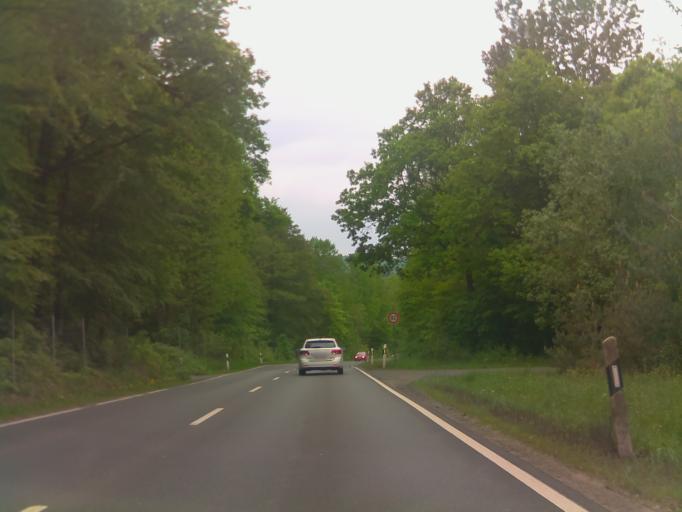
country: DE
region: Hesse
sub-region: Regierungsbezirk Darmstadt
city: Kronberg
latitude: 50.1946
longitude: 8.5218
